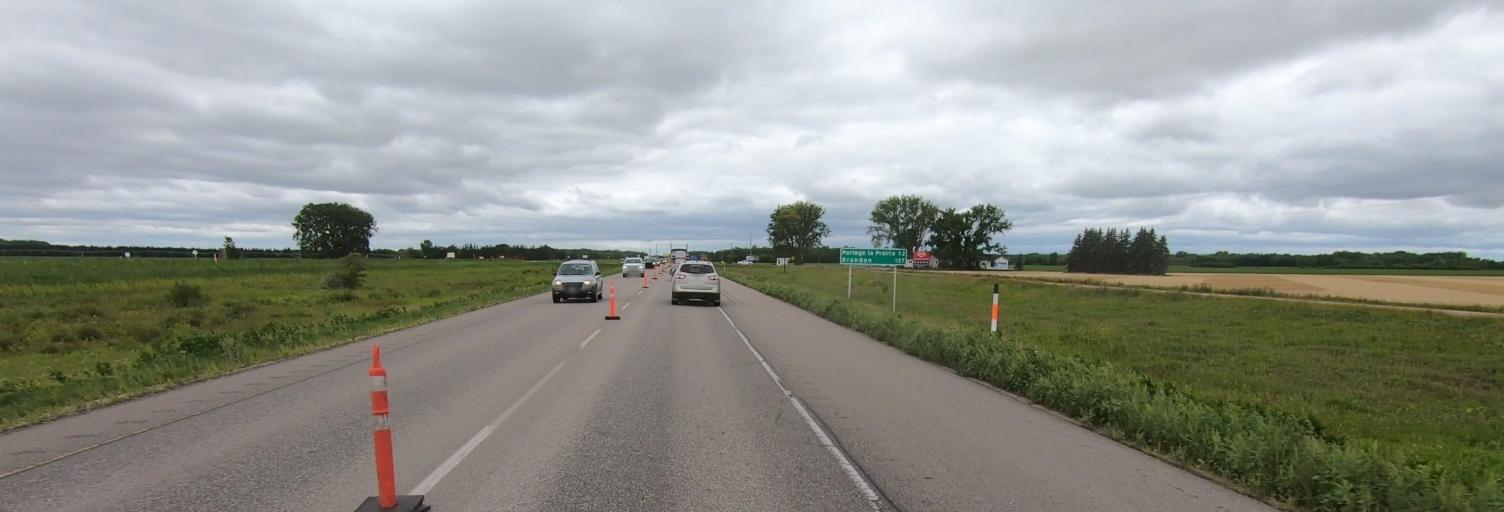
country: CA
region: Manitoba
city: Portage la Prairie
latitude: 49.9727
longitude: -98.1117
